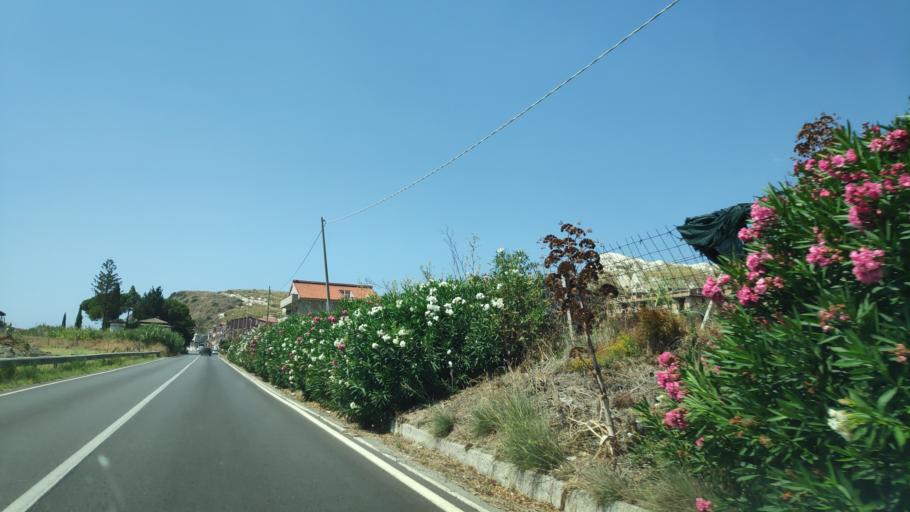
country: IT
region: Calabria
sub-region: Provincia di Reggio Calabria
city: Weather Station
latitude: 37.9335
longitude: 16.0703
